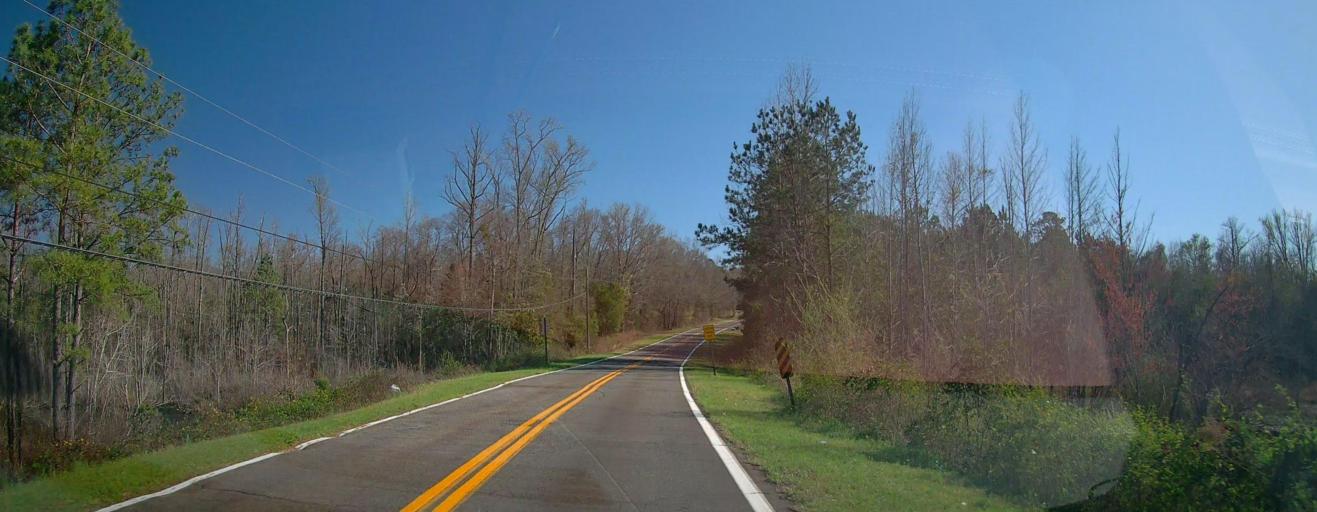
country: US
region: Georgia
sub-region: Peach County
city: Fort Valley
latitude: 32.6196
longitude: -83.8951
